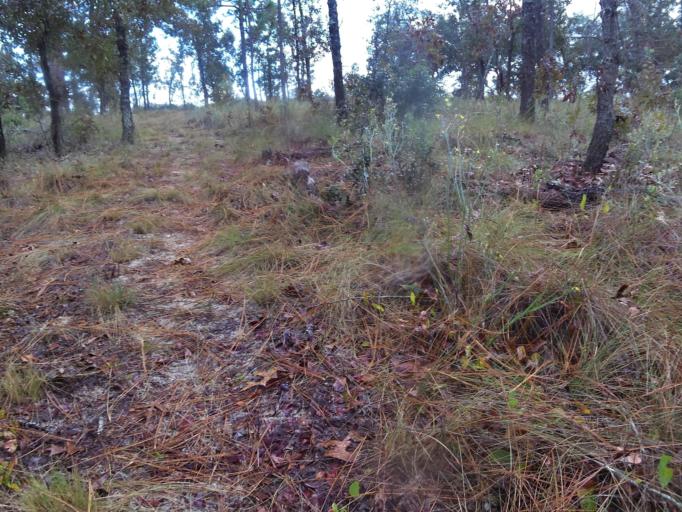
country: US
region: Florida
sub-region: Clay County
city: Keystone Heights
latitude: 29.8359
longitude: -81.9688
